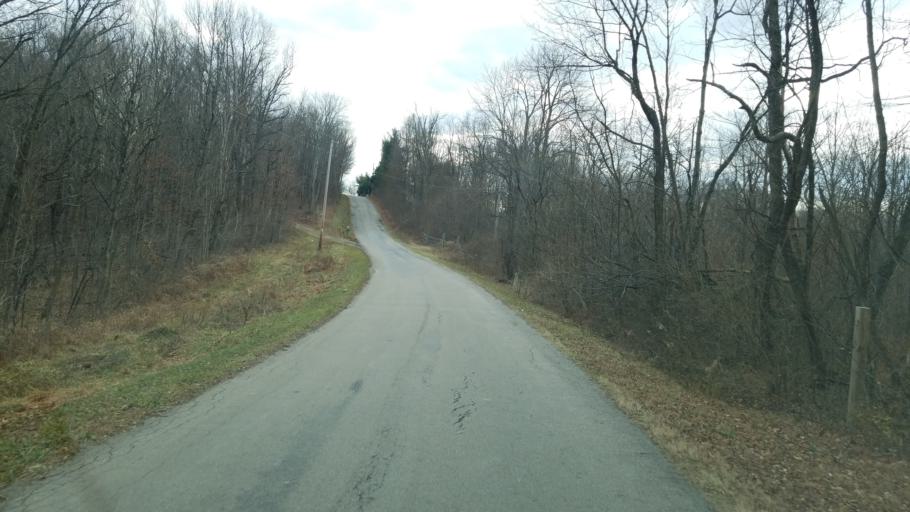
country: US
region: Ohio
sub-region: Highland County
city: Greenfield
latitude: 39.1915
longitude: -83.2687
